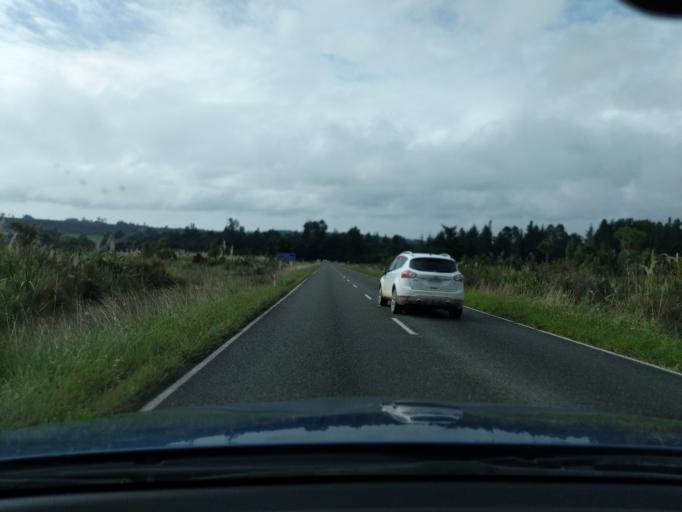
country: NZ
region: Tasman
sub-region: Tasman District
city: Takaka
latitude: -40.6786
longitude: 172.6639
